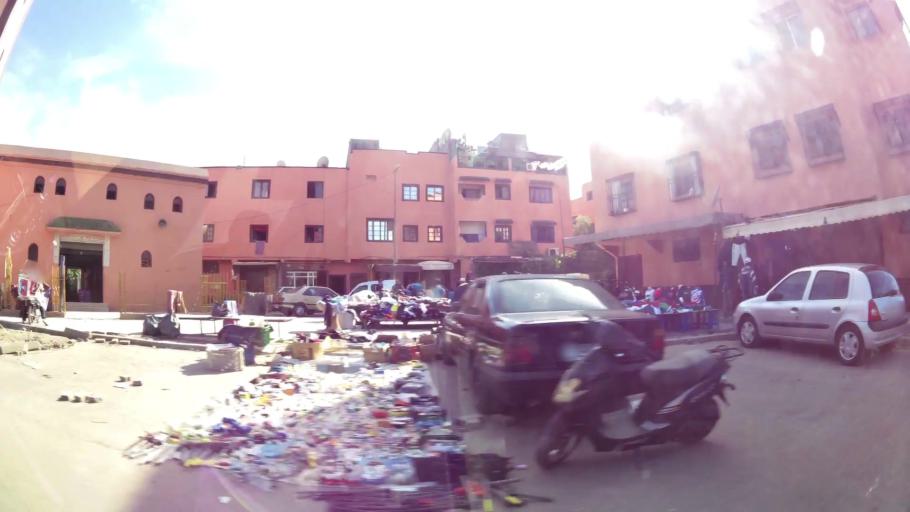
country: MA
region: Marrakech-Tensift-Al Haouz
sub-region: Marrakech
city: Marrakesh
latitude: 31.6512
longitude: -8.0241
